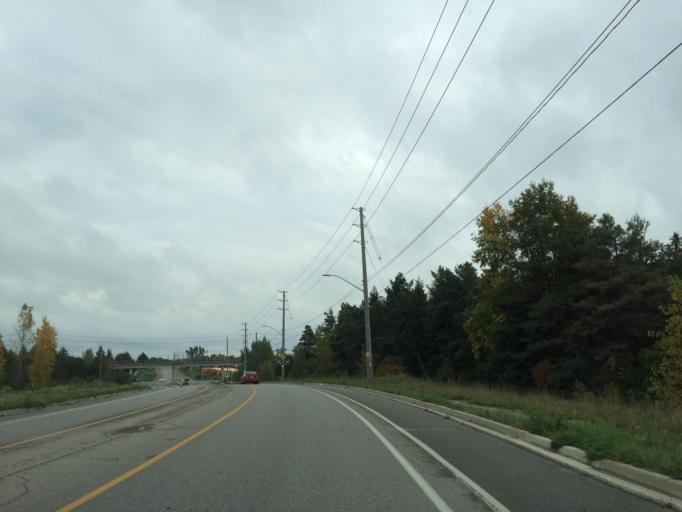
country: CA
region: Ontario
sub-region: Wellington County
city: Guelph
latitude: 43.5642
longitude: -80.2118
